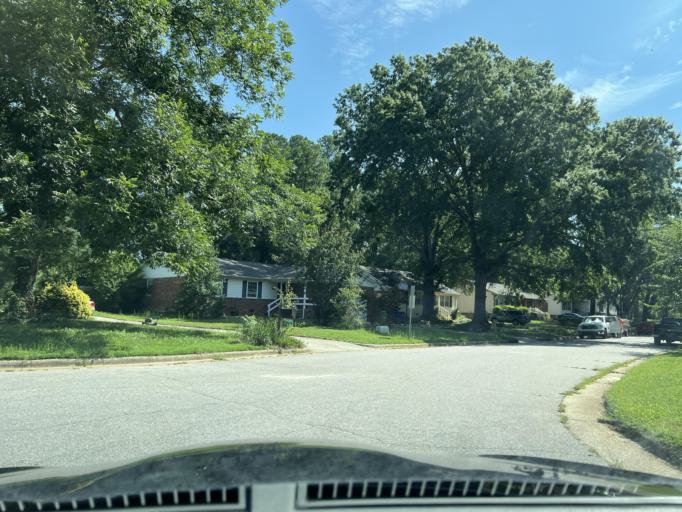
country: US
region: North Carolina
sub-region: Wake County
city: West Raleigh
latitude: 35.8685
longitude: -78.6043
